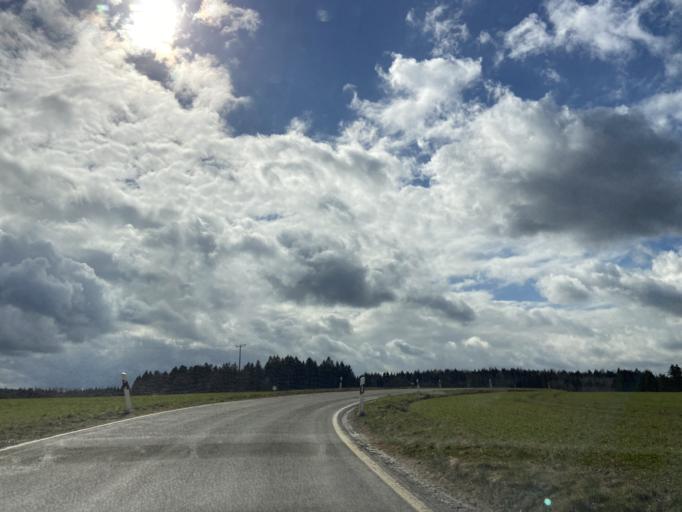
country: DE
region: Baden-Wuerttemberg
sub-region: Tuebingen Region
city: Pfullendorf
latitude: 47.9624
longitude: 9.3052
